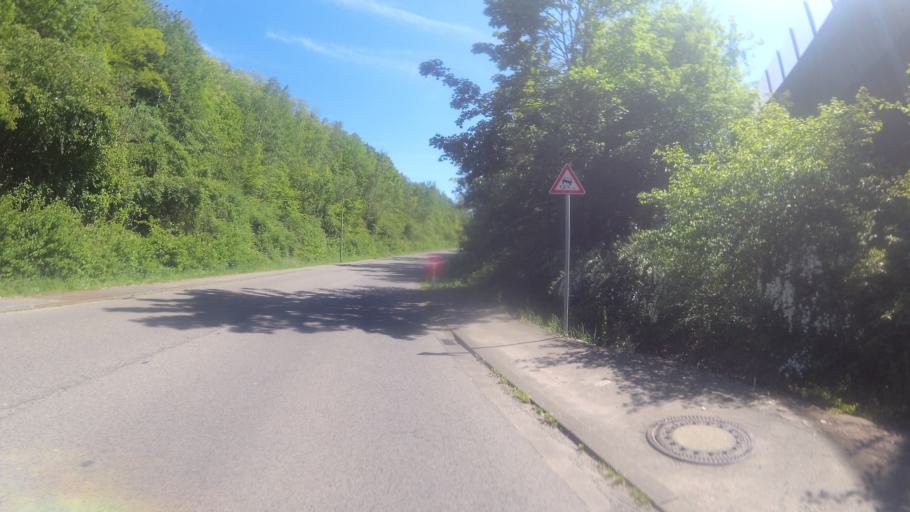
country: DE
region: Saarland
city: Quierschied
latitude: 49.3290
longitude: 7.0574
